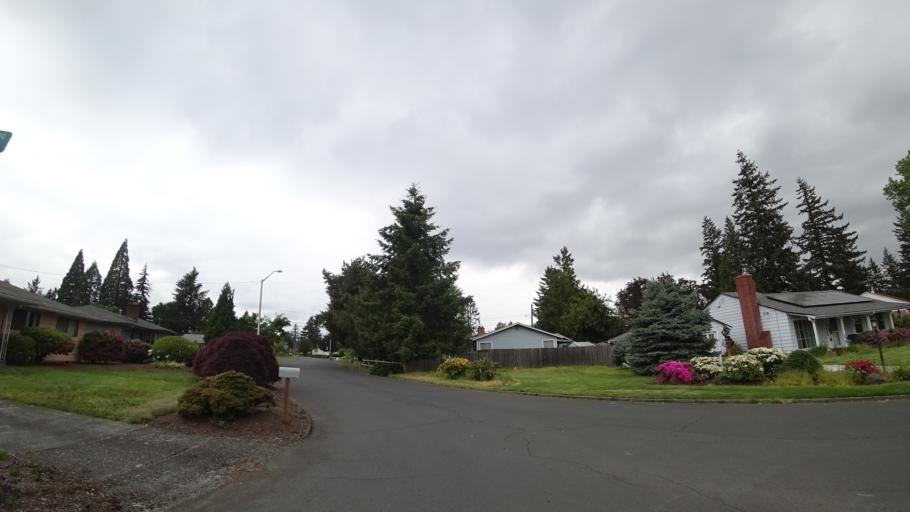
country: US
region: Oregon
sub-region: Multnomah County
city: Lents
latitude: 45.5133
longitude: -122.5184
